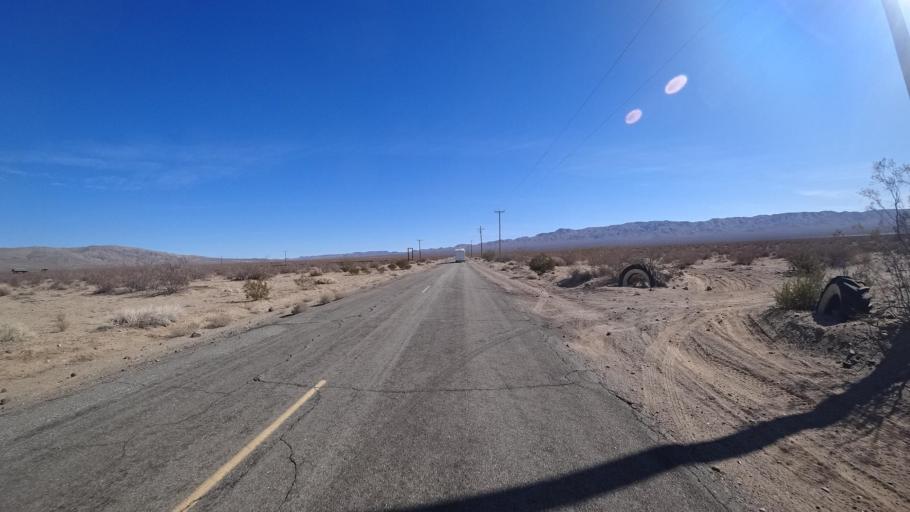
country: US
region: California
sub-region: Kern County
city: China Lake Acres
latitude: 35.3916
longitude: -117.7909
